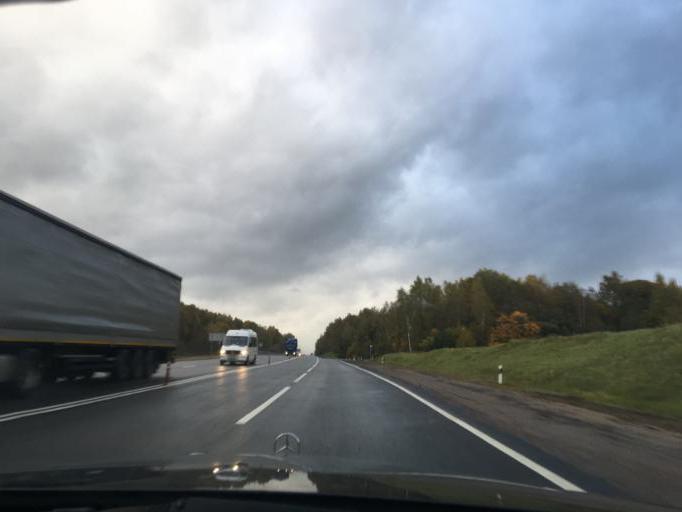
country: RU
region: Smolensk
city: Pechersk
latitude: 54.8980
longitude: 32.1185
